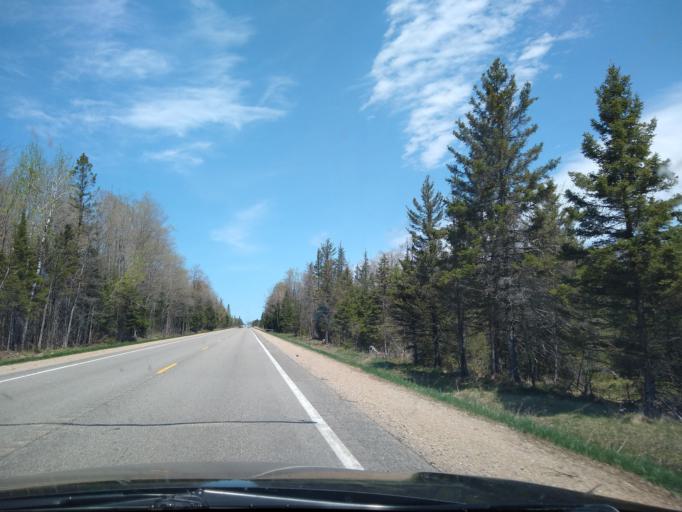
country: US
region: Michigan
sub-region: Delta County
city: Gladstone
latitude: 46.0667
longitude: -86.9811
